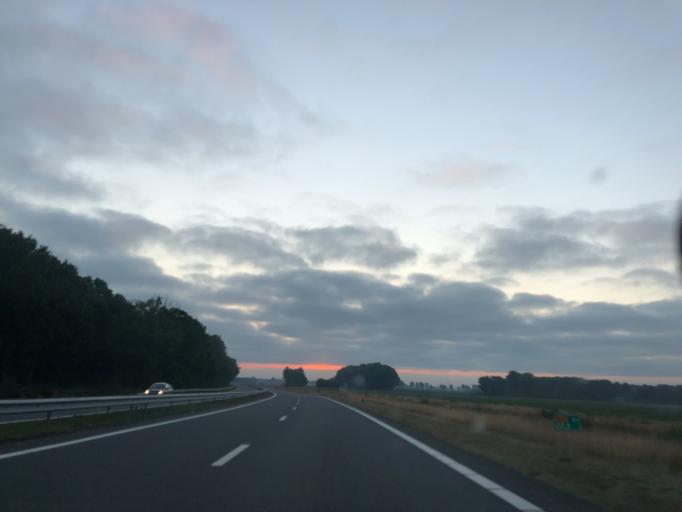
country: NL
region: Drenthe
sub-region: Gemeente Aa en Hunze
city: Anloo
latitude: 53.0137
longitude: 6.7637
